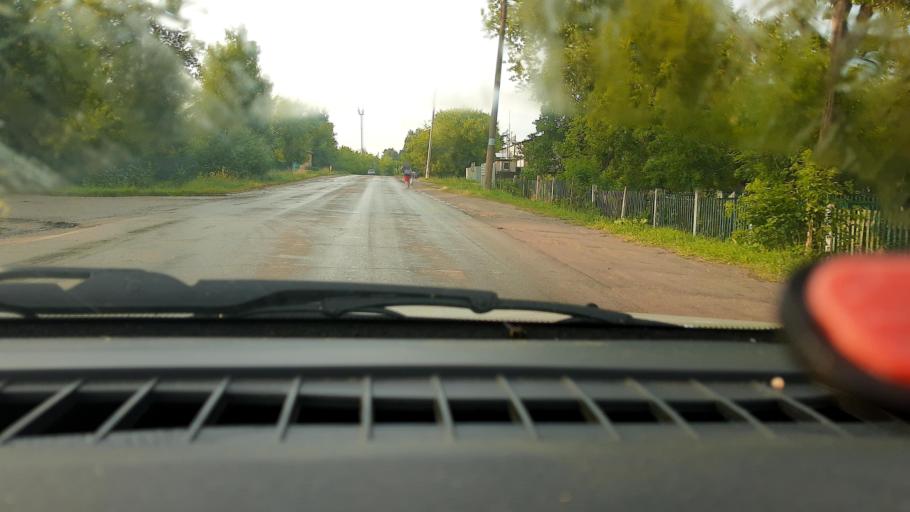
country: RU
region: Nizjnij Novgorod
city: Lukoyanov
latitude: 55.0414
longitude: 44.4972
